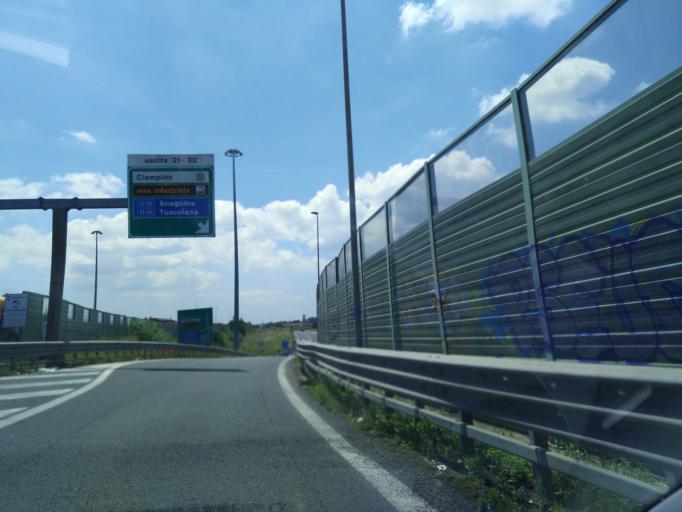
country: IT
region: Latium
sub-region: Citta metropolitana di Roma Capitale
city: Ciampino
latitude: 41.8351
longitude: 12.5882
